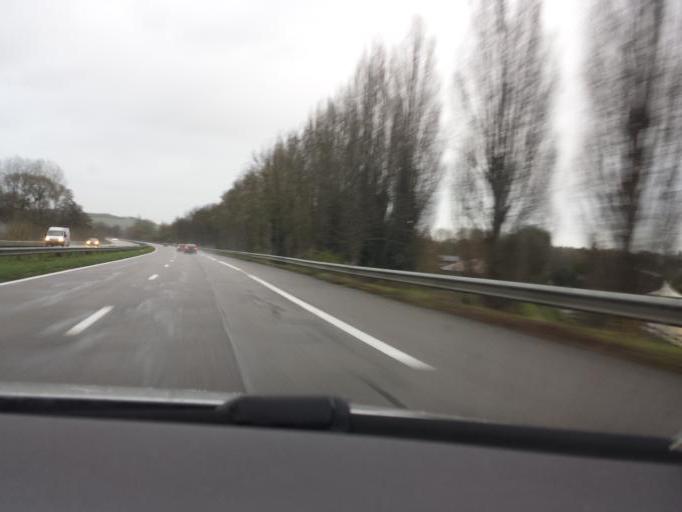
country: FR
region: Haute-Normandie
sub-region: Departement de l'Eure
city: Pacy-sur-Eure
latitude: 49.0086
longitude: 1.3638
